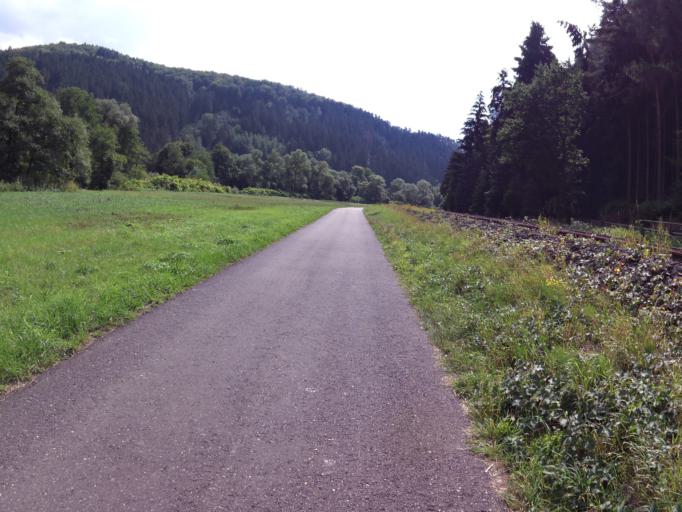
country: DE
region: Rheinland-Pfalz
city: Kordel
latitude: 49.8309
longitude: 6.6502
